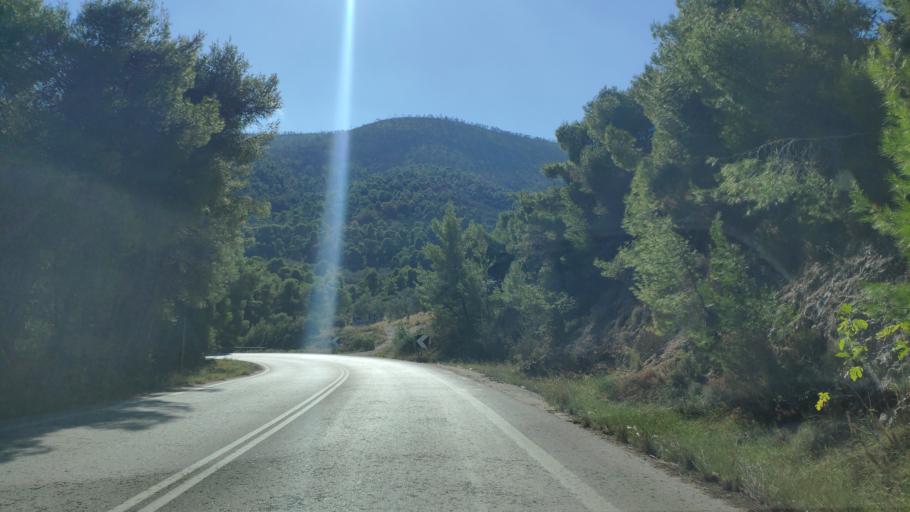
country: GR
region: Peloponnese
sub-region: Nomos Korinthias
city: Sofikon
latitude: 37.8302
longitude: 23.0286
